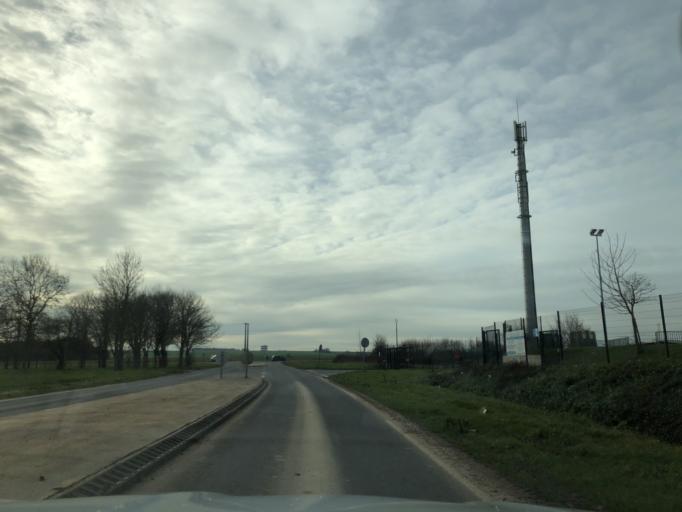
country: FR
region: Lower Normandy
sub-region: Departement du Calvados
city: Hermanville-sur-Mer
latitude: 49.2850
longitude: -0.3282
